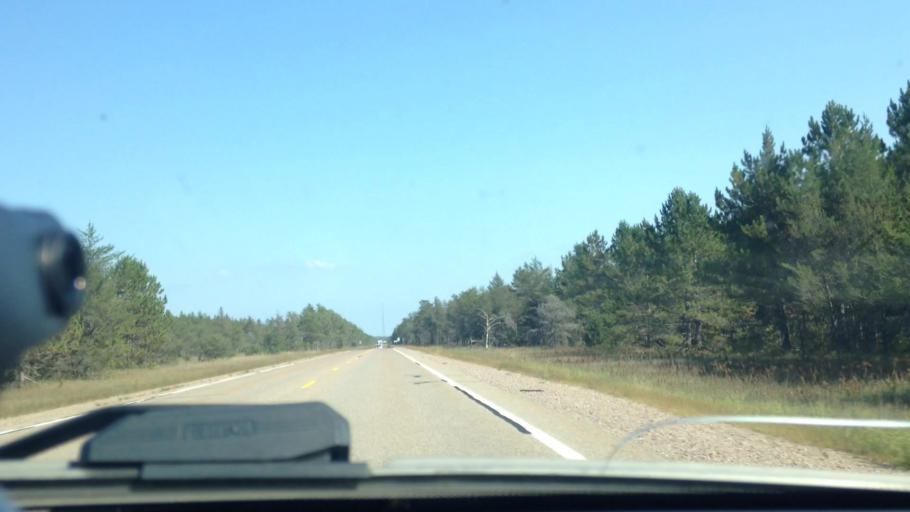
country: US
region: Michigan
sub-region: Chippewa County
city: Sault Ste. Marie
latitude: 46.3587
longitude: -84.8268
